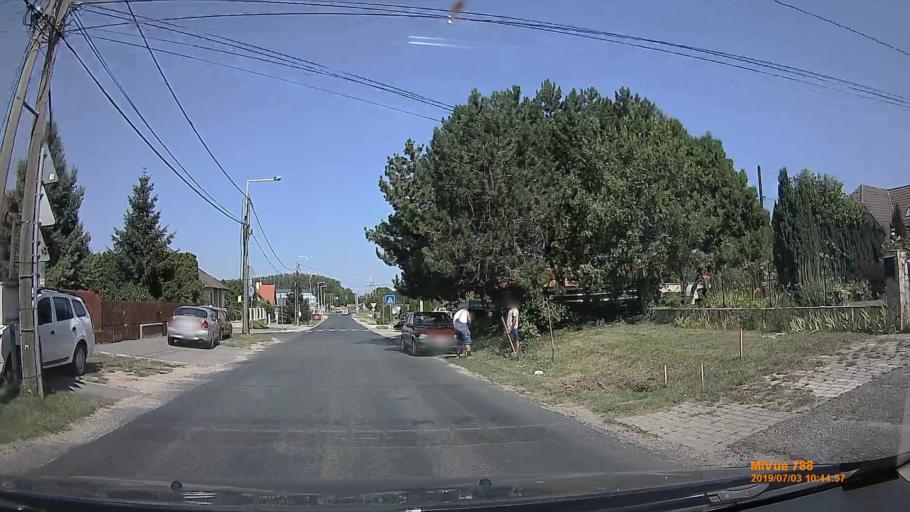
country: HU
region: Gyor-Moson-Sopron
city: Gyorujbarat
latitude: 47.6367
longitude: 17.6060
